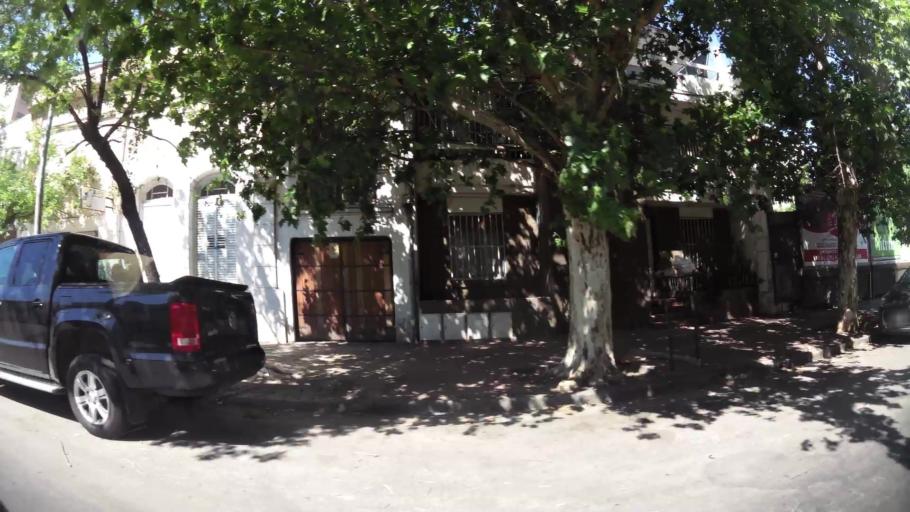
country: AR
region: Cordoba
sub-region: Departamento de Capital
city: Cordoba
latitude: -31.4117
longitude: -64.1721
